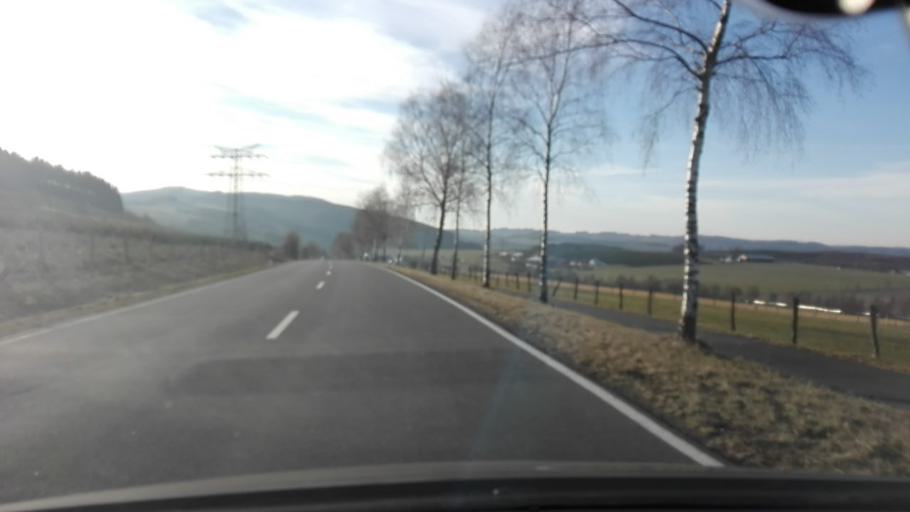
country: DE
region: North Rhine-Westphalia
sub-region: Regierungsbezirk Arnsberg
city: Schmallenberg
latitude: 51.1553
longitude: 8.2665
